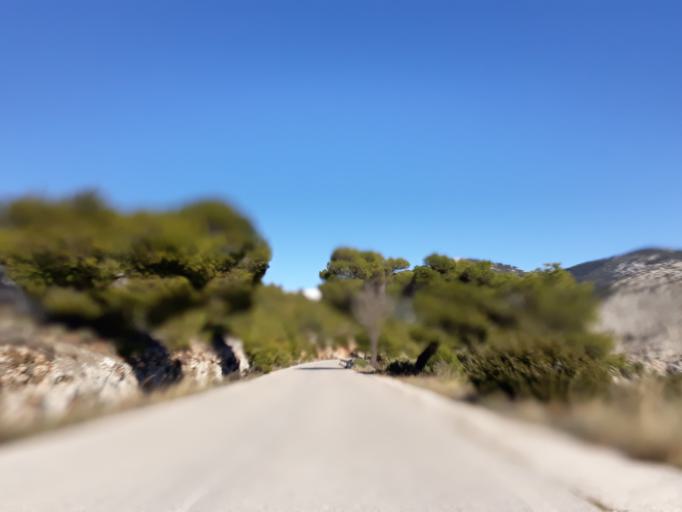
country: GR
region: Attica
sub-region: Nomarchia Dytikis Attikis
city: Fyli
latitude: 38.1180
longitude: 23.6487
